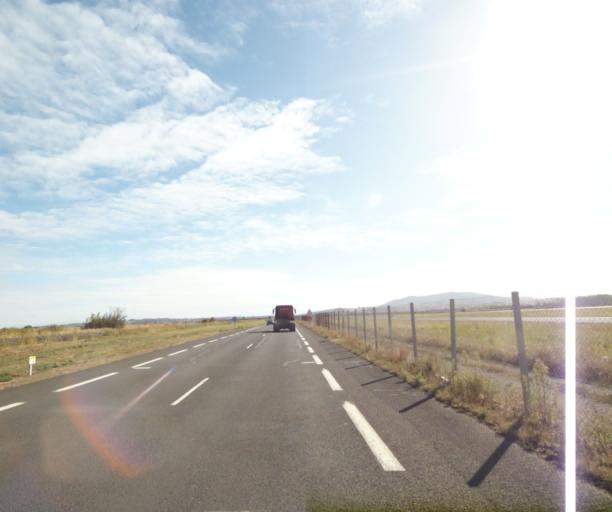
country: FR
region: Auvergne
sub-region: Departement du Puy-de-Dome
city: Aulnat
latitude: 45.7908
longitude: 3.1848
